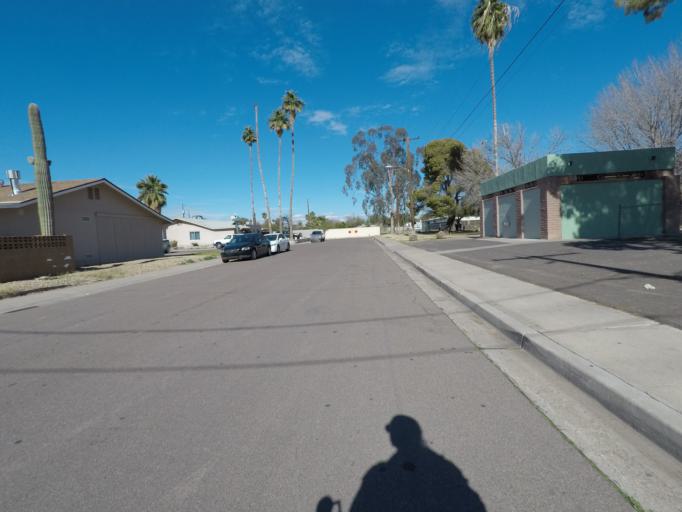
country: US
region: Arizona
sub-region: Maricopa County
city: Tempe Junction
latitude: 33.4095
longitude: -111.9500
